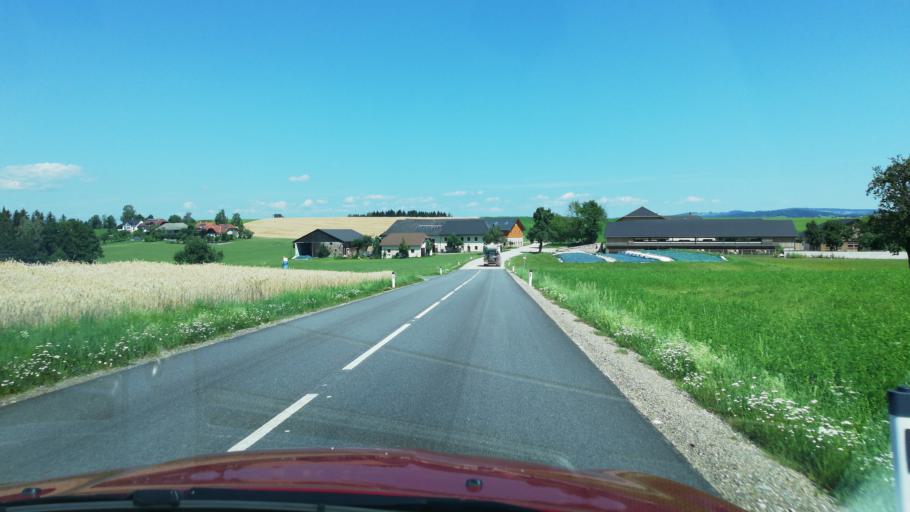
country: AT
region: Upper Austria
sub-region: Politischer Bezirk Urfahr-Umgebung
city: Herzogsdorf
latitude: 48.4741
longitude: 14.0609
